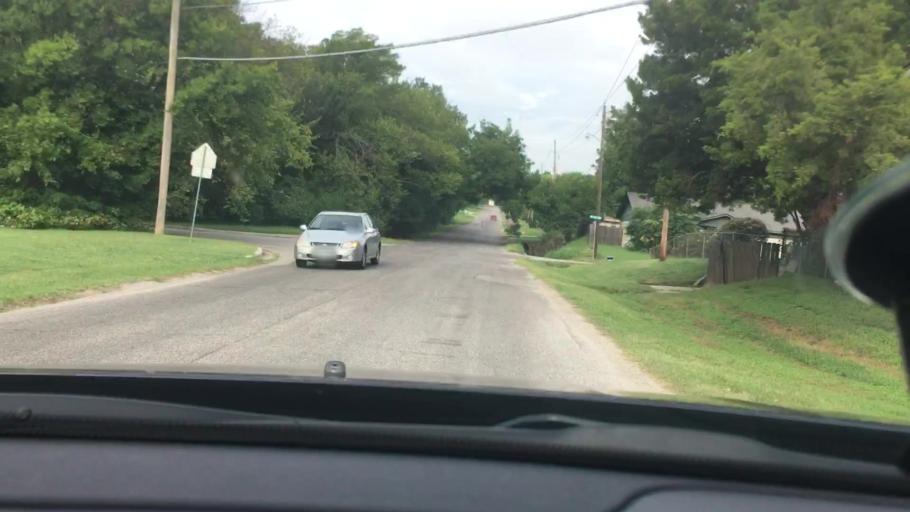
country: US
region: Oklahoma
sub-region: Carter County
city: Ardmore
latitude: 34.1874
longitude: -97.1260
